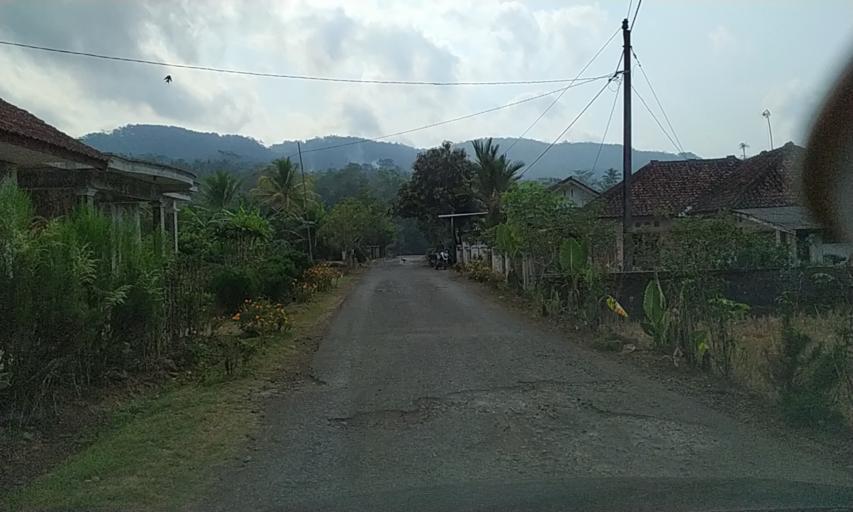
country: ID
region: Central Java
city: Dayeuhluhur
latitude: -7.2597
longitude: 108.6170
